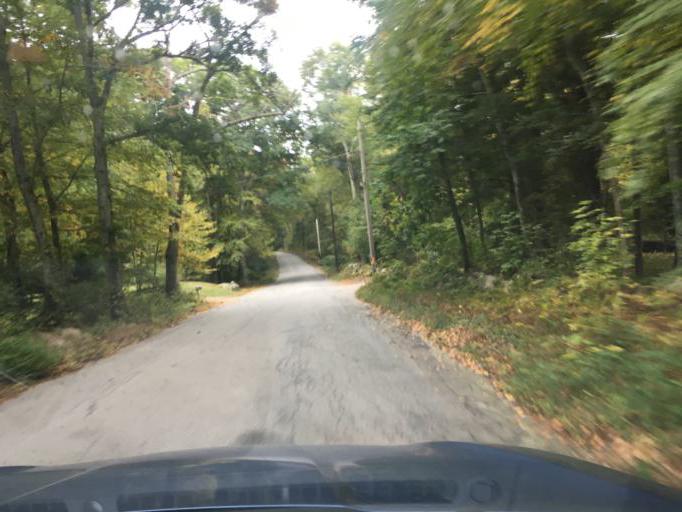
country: US
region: Rhode Island
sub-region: Washington County
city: Exeter
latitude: 41.6236
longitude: -71.5531
